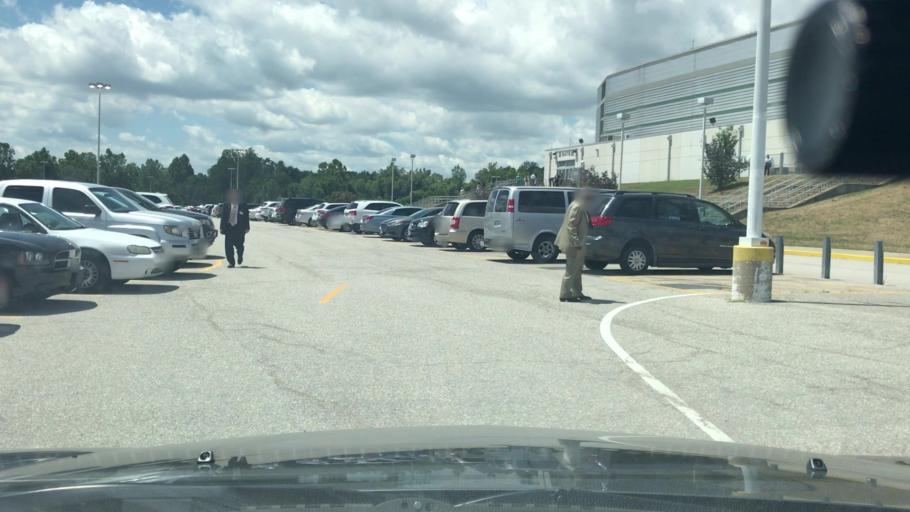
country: US
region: Missouri
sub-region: Saint Charles County
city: Saint Charles
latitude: 38.7476
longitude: -90.5080
